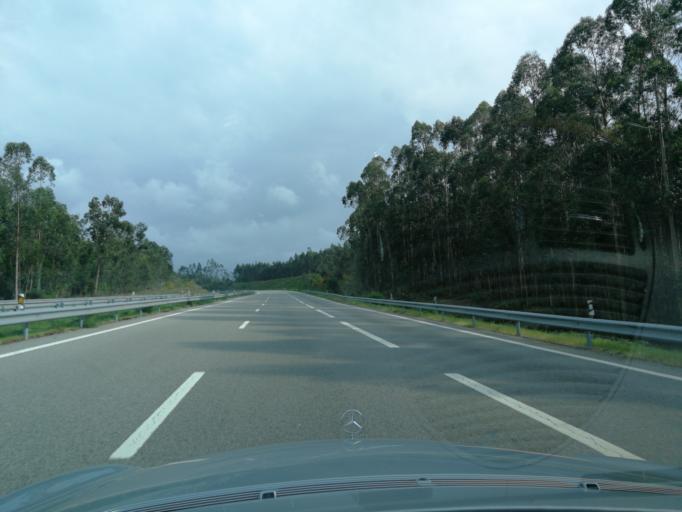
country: PT
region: Porto
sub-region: Vila do Conde
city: Arvore
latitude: 41.3832
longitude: -8.6652
